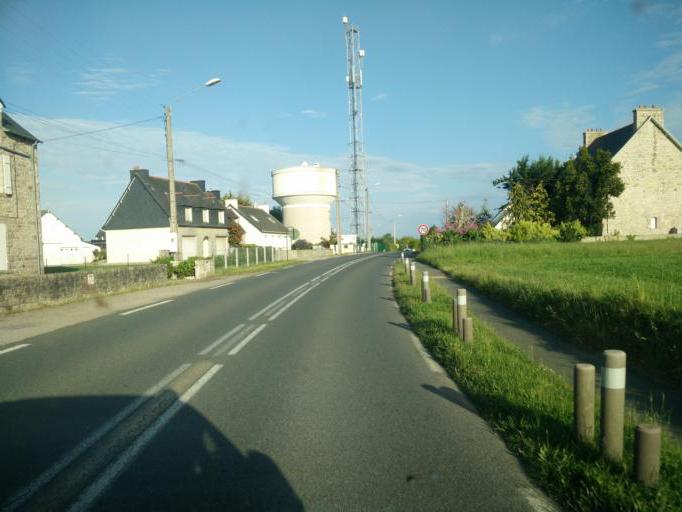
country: FR
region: Brittany
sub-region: Departement des Cotes-d'Armor
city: Erquy
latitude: 48.6259
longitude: -2.4483
